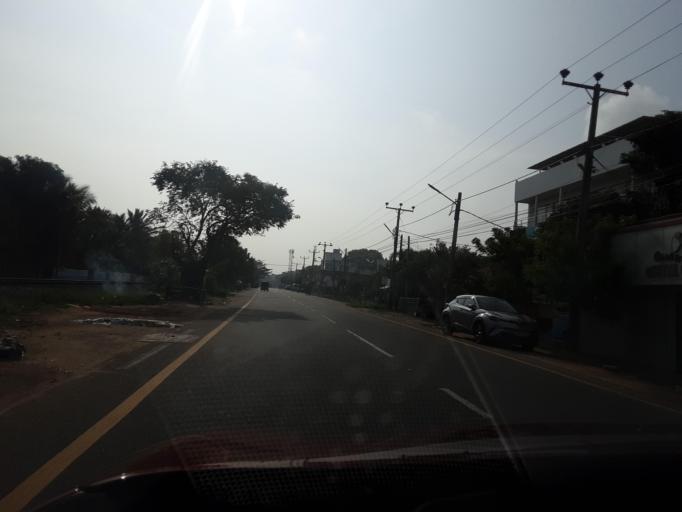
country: LK
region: Northern Province
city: Valvedditturai
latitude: 9.6616
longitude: 80.1679
